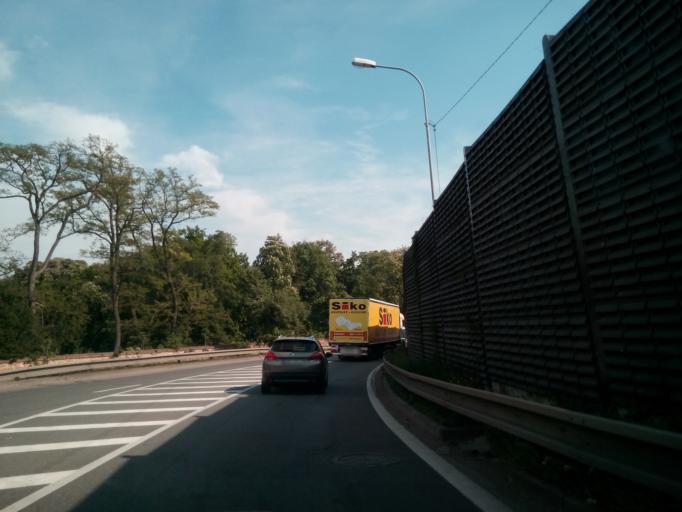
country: CZ
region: South Moravian
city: Slavkov u Brna
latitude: 49.1554
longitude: 16.8648
